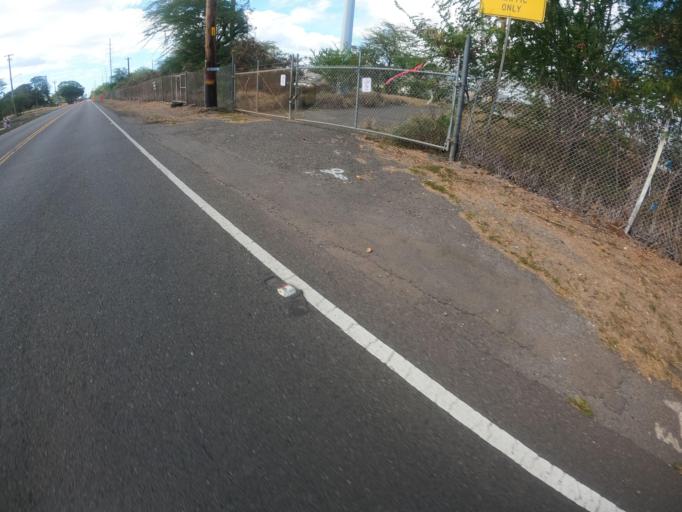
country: US
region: Hawaii
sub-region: Honolulu County
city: Makakilo City
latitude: 21.3231
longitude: -158.0787
